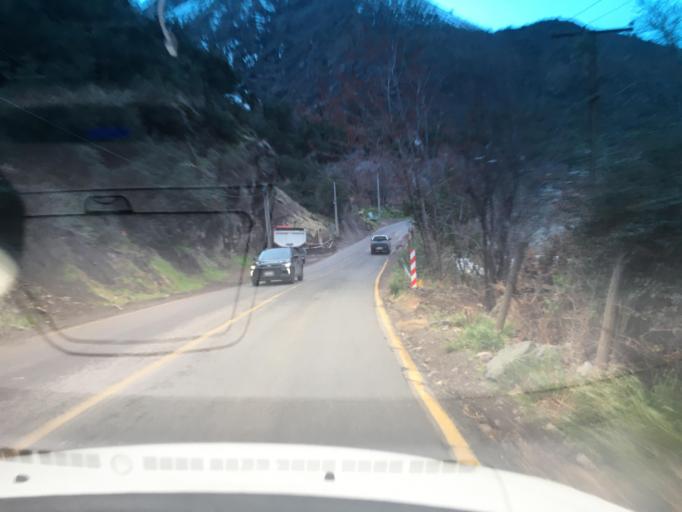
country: CL
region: Santiago Metropolitan
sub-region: Provincia de Cordillera
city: Puente Alto
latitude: -33.7329
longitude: -70.3042
